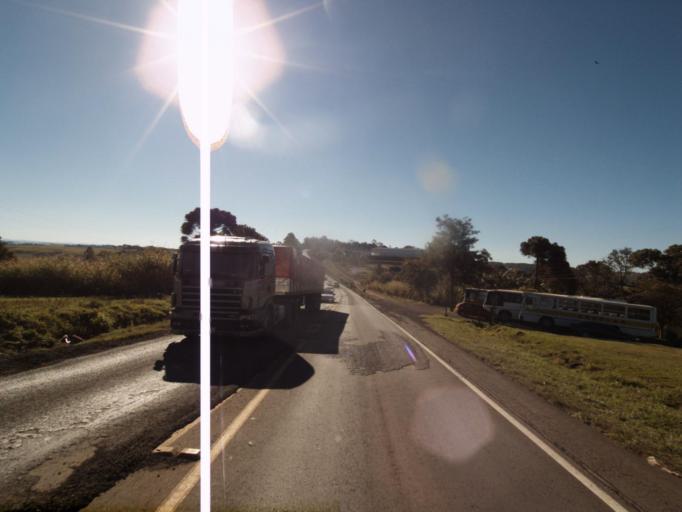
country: AR
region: Misiones
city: Bernardo de Irigoyen
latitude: -26.6781
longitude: -53.5156
